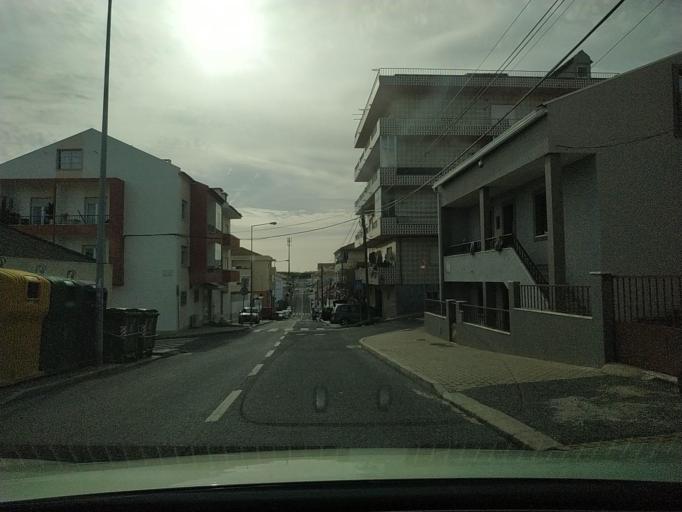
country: PT
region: Lisbon
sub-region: Amadora
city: Amadora
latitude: 38.7755
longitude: -9.2346
